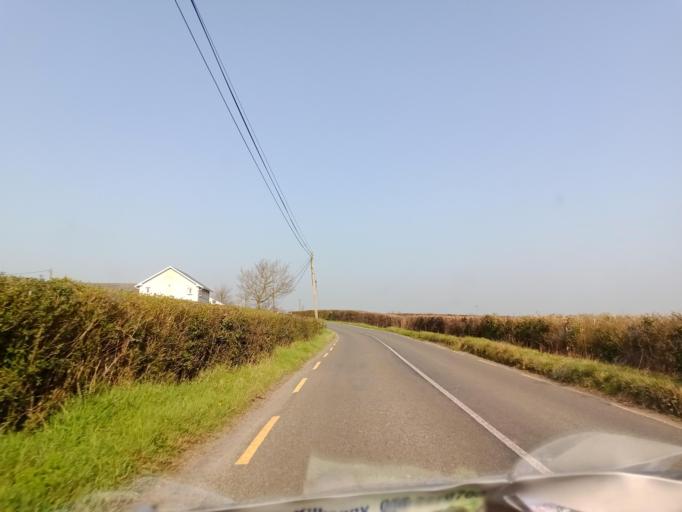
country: IE
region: Leinster
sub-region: Kilkenny
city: Callan
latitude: 52.5301
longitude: -7.3829
